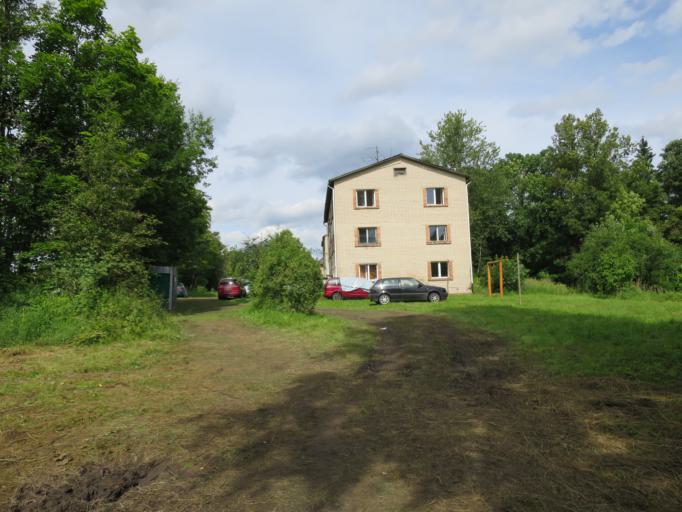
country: LV
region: Ligatne
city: Ligatne
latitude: 57.2219
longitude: 24.9638
